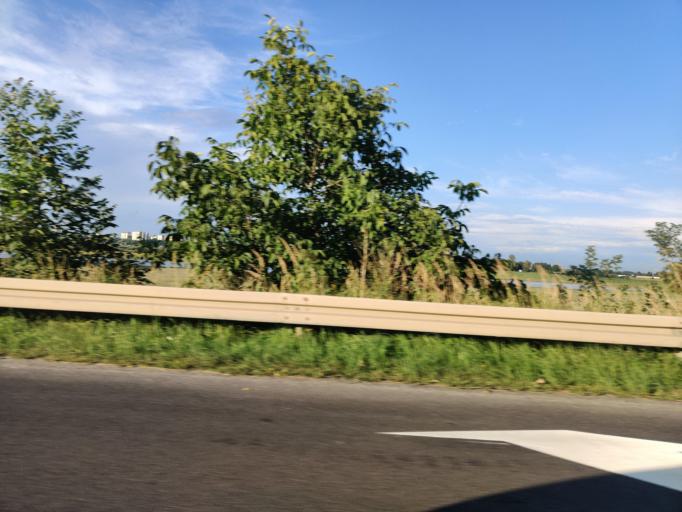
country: PL
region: Greater Poland Voivodeship
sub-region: Konin
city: Konin
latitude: 52.2112
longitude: 18.2614
